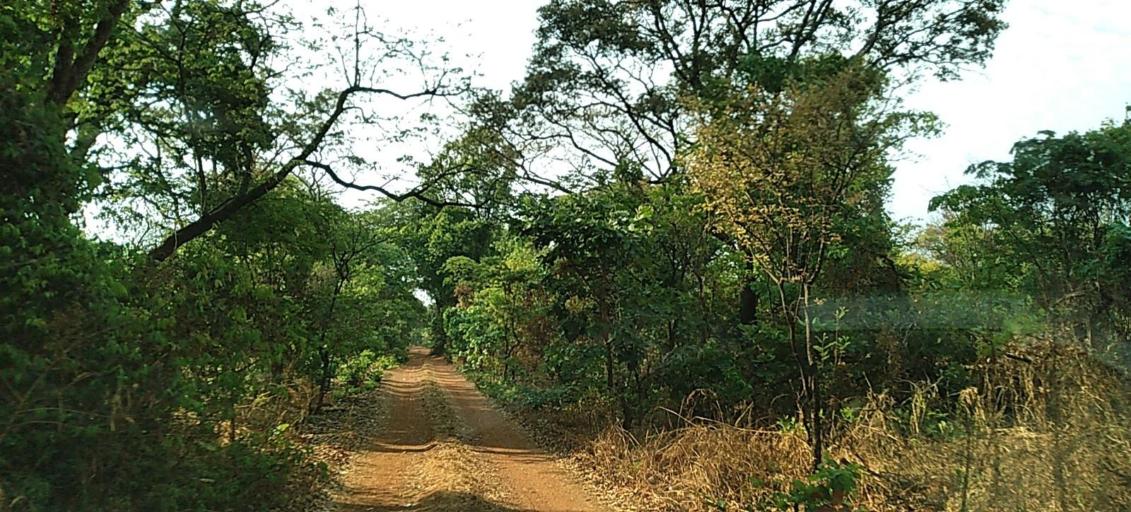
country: ZM
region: Copperbelt
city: Kalulushi
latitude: -12.9768
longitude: 27.7160
